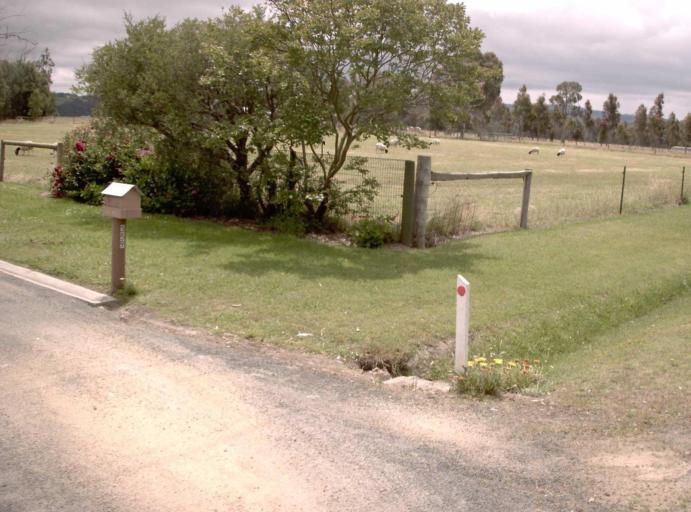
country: AU
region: Victoria
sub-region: Latrobe
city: Traralgon
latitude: -38.5395
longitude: 146.6569
